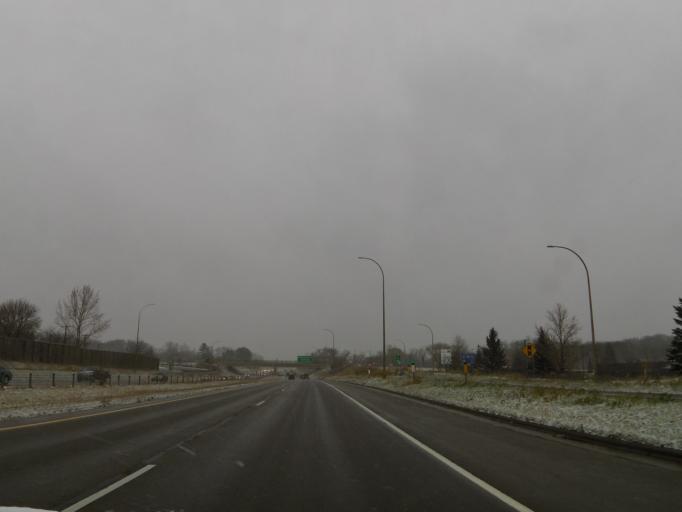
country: US
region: Minnesota
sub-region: Hennepin County
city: Edina
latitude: 44.8337
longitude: -93.3981
